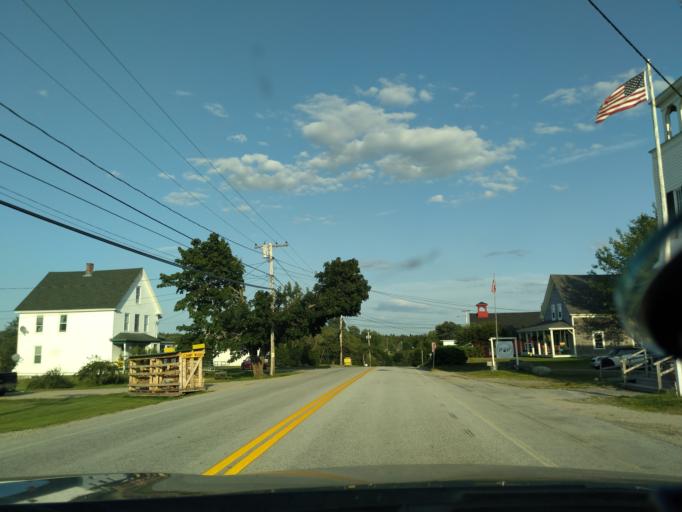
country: US
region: Maine
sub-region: Hancock County
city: Gouldsboro
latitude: 44.3898
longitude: -68.0413
